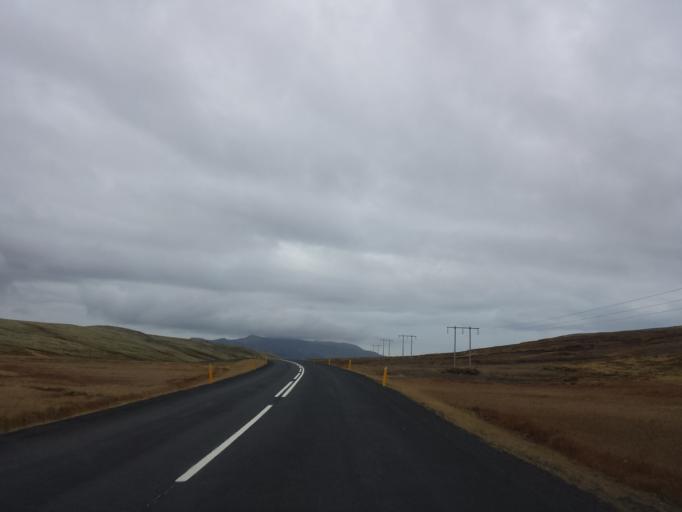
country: IS
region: West
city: Stykkisholmur
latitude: 64.9193
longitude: -22.8784
